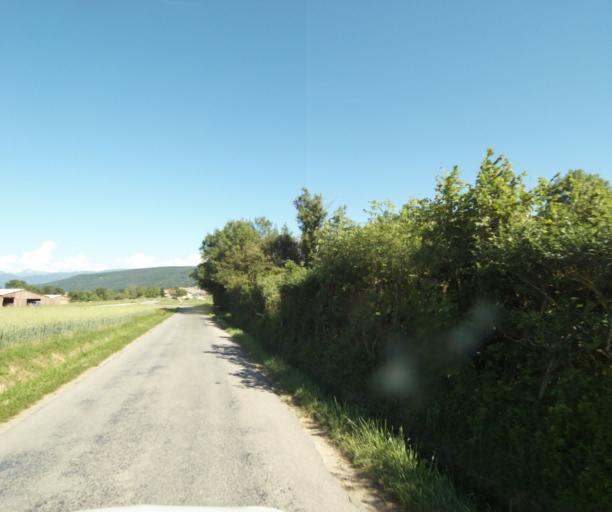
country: FR
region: Rhone-Alpes
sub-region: Departement de la Haute-Savoie
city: Massongy
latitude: 46.3263
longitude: 6.3144
